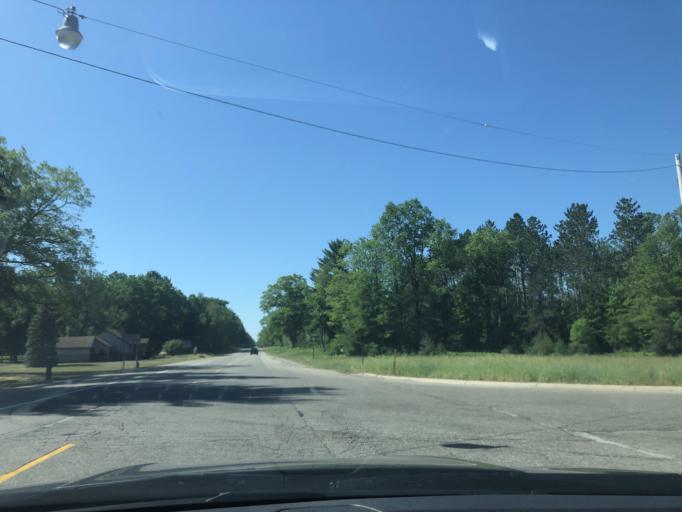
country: US
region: Michigan
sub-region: Missaukee County
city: Lake City
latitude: 44.3683
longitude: -85.2163
